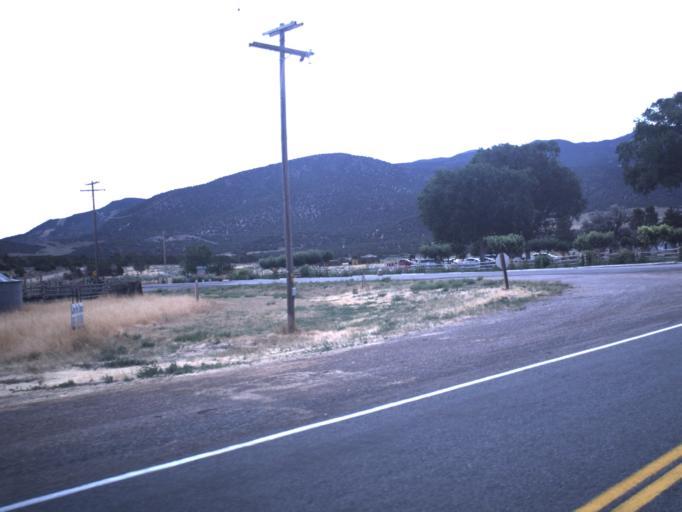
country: US
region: Utah
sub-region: Beaver County
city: Beaver
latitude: 38.6020
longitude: -112.5821
